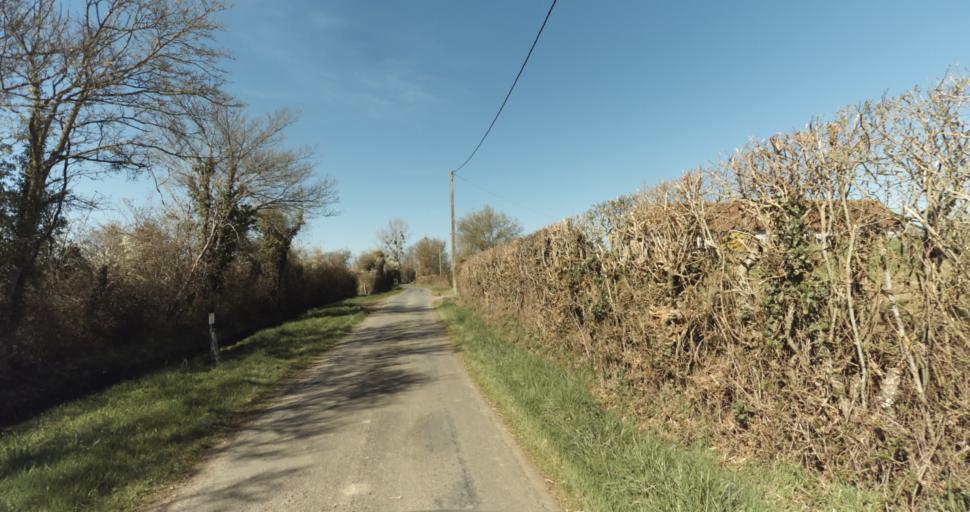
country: FR
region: Lower Normandy
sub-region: Departement du Calvados
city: Saint-Pierre-sur-Dives
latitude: 49.0582
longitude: -0.0254
